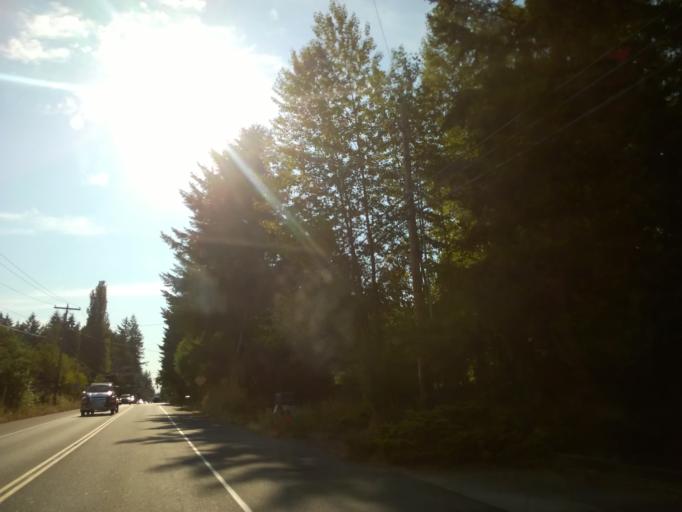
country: US
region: Washington
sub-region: King County
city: Cottage Lake
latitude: 47.7615
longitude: -122.1103
